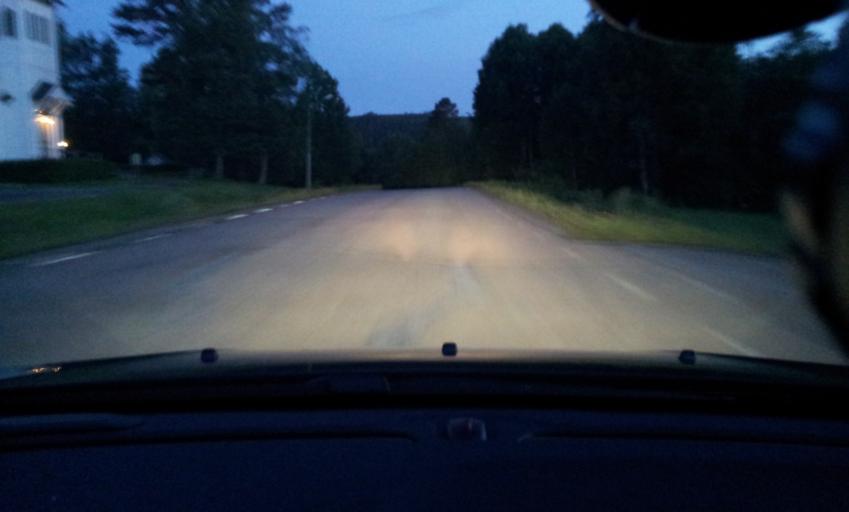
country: SE
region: Jaemtland
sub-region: Bergs Kommun
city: Hoverberg
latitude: 62.6649
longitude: 14.7492
